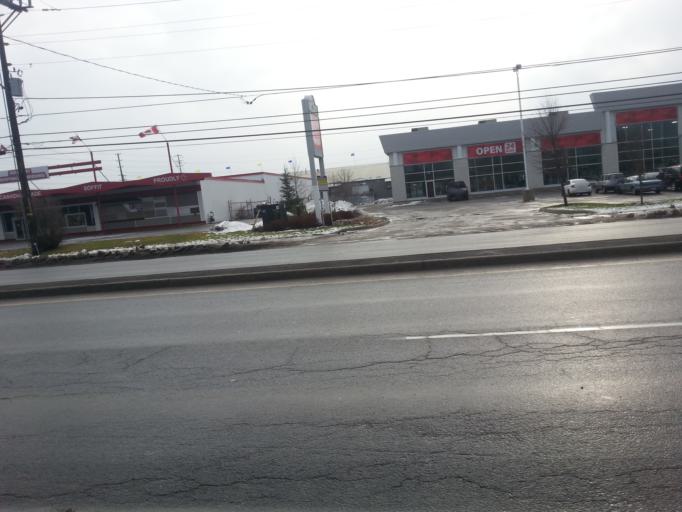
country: CA
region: Ontario
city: Greater Sudbury
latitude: 46.5221
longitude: -80.9243
